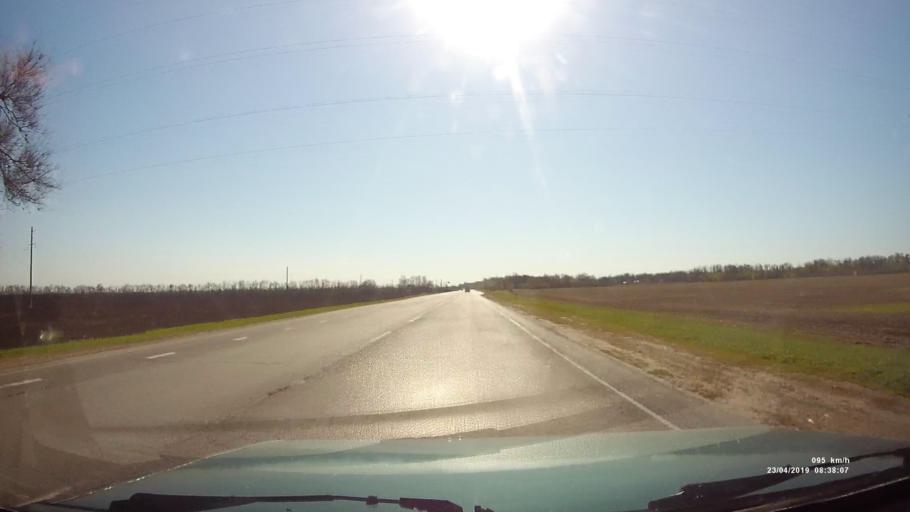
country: RU
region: Rostov
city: Tselina
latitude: 46.5316
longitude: 41.1815
